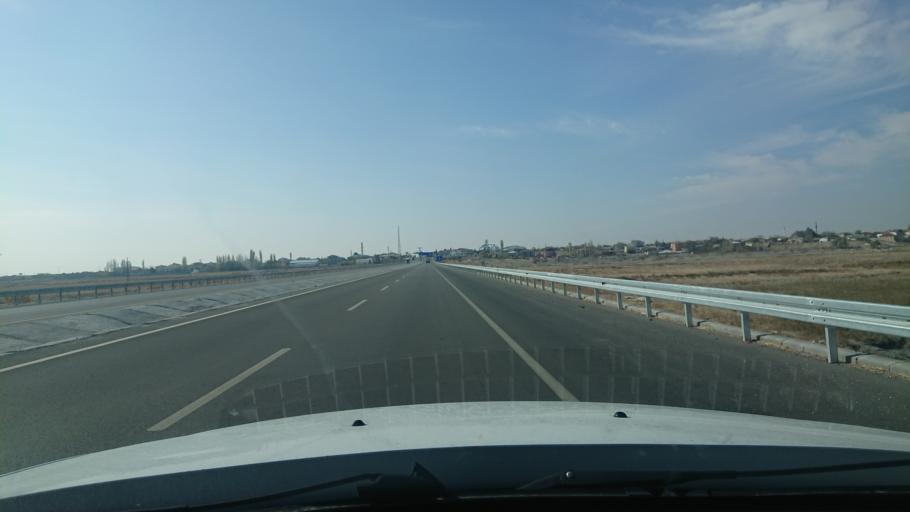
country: TR
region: Aksaray
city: Sultanhani
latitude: 38.2500
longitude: 33.4587
